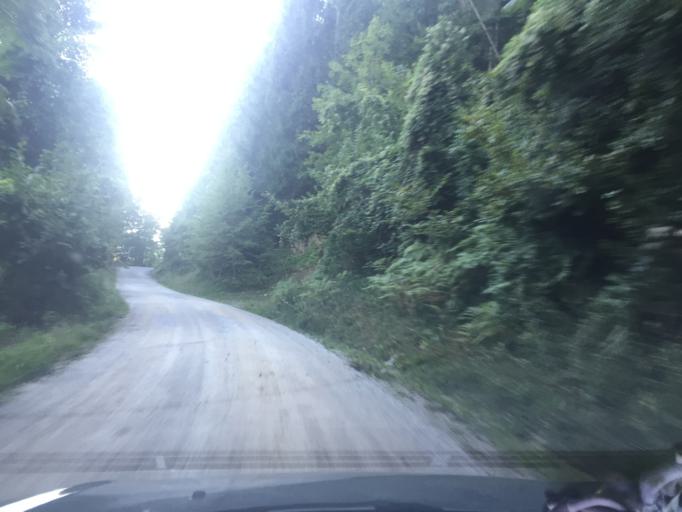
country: SI
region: Sostanj
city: Topolsica
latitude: 46.4555
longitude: 14.9972
